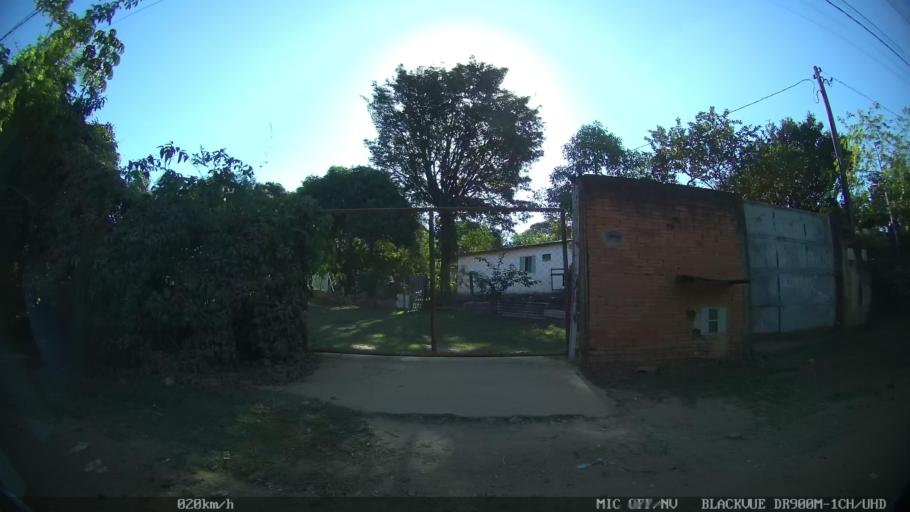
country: BR
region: Sao Paulo
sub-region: Franca
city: Franca
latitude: -20.4818
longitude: -47.4213
